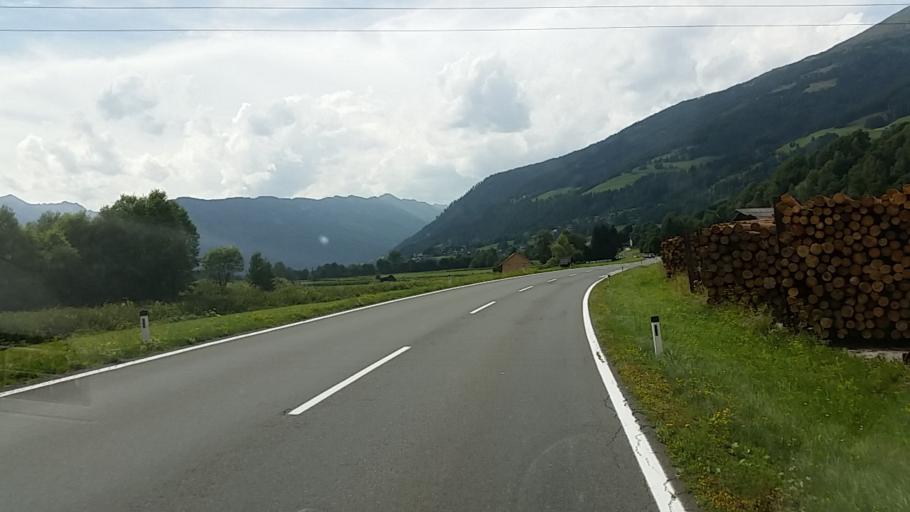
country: AT
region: Salzburg
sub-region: Politischer Bezirk Tamsweg
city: Sankt Margarethen im Lungau
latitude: 47.0947
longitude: 13.6678
